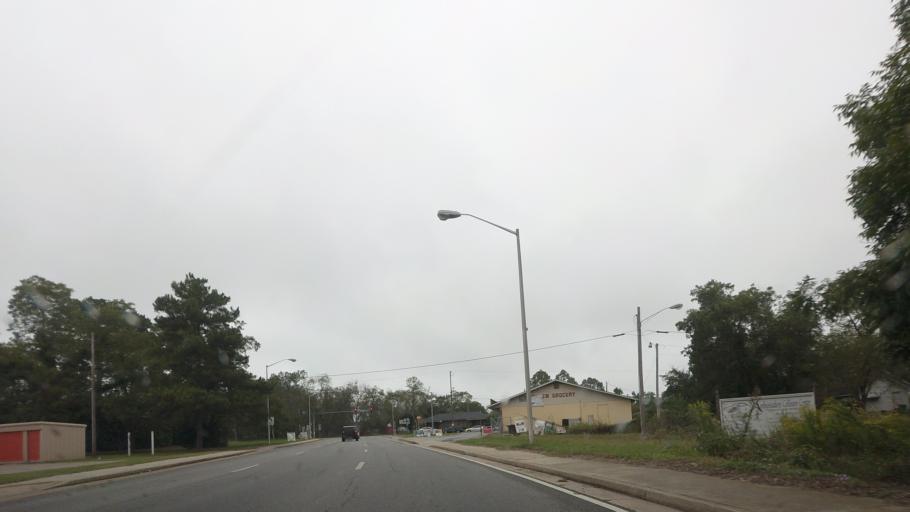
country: US
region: Georgia
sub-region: Ben Hill County
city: Fitzgerald
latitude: 31.7231
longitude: -83.2518
